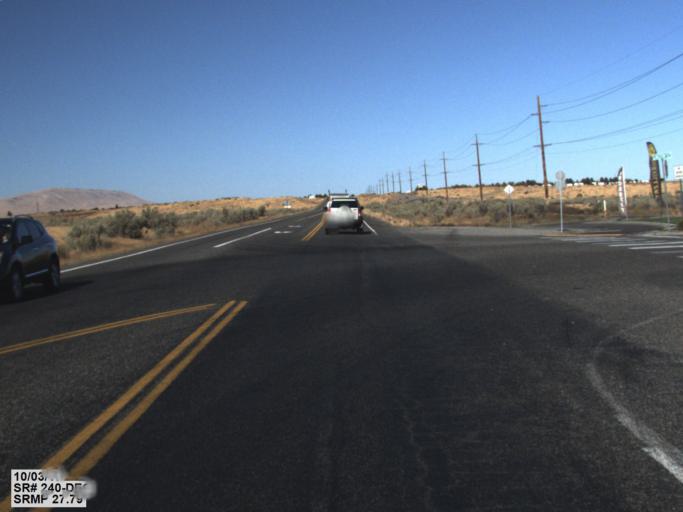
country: US
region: Washington
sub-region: Benton County
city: Richland
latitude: 46.3183
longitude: -119.3019
